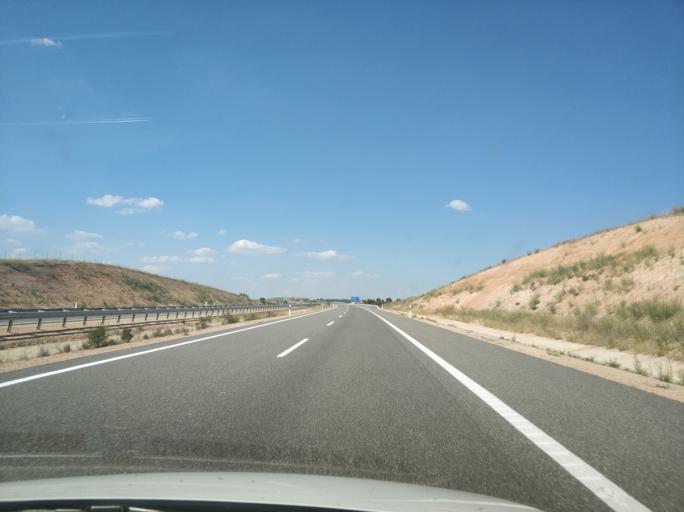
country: ES
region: Castille and Leon
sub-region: Provincia de Zamora
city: Granja de Moreruela
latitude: 41.8169
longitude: -5.7458
